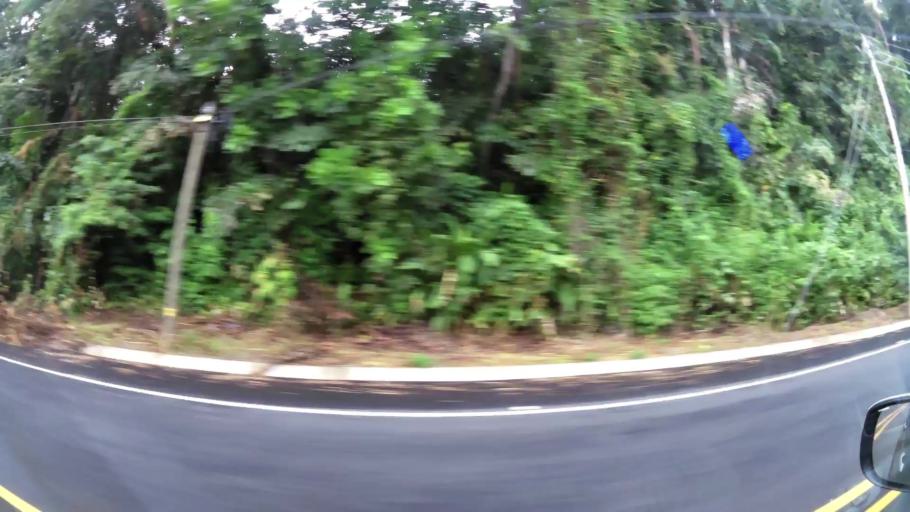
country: CR
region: Alajuela
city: Orotina
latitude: 9.9482
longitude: -84.5707
